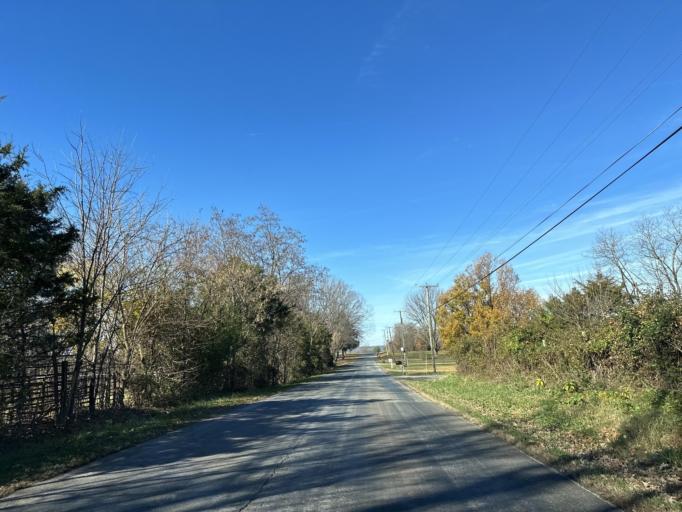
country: US
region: Virginia
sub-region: Augusta County
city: Weyers Cave
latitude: 38.2133
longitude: -78.9031
